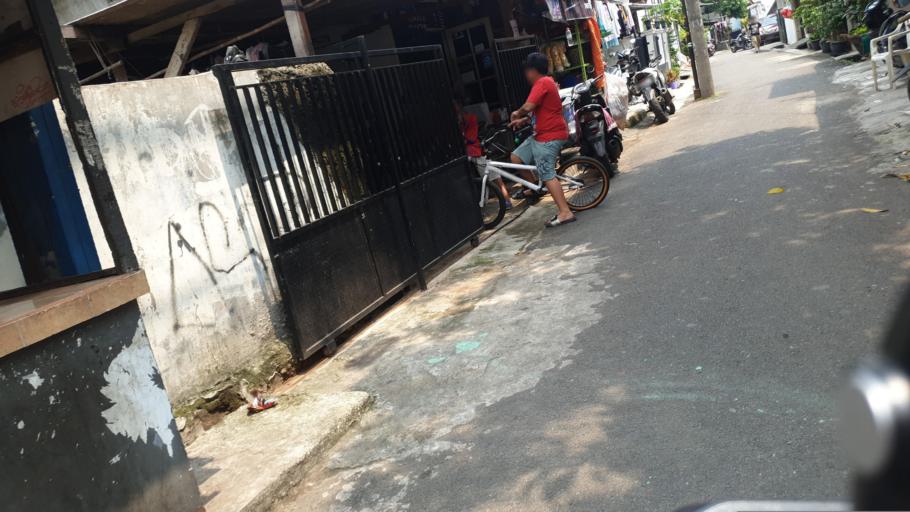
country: ID
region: West Java
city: Ciputat
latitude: -6.1922
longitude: 106.7538
